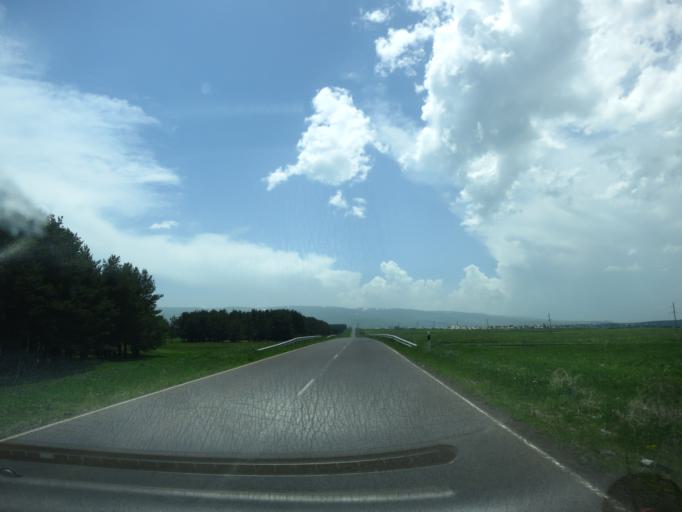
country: GE
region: Samtskhe-Javakheti
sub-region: Ninotsminda
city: Ninotsminda
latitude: 41.2874
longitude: 43.6356
